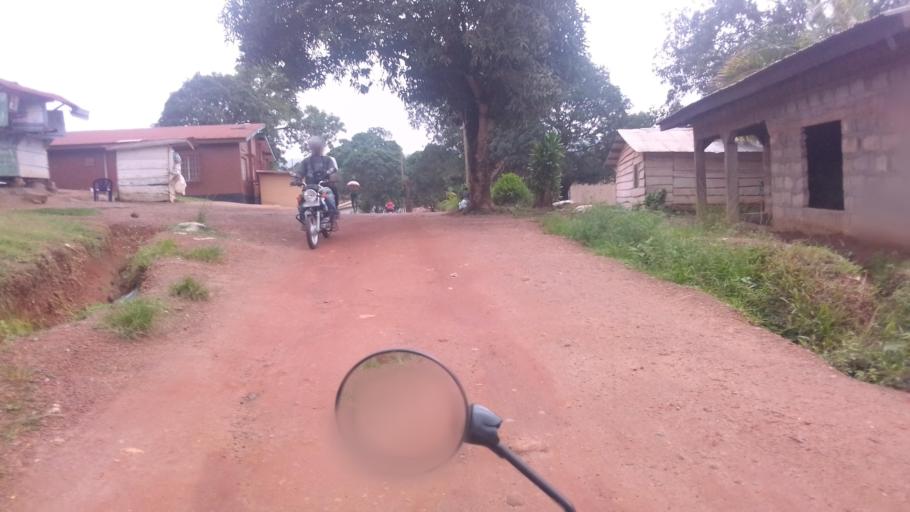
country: SL
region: Eastern Province
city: Kenema
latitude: 7.8694
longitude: -11.1770
